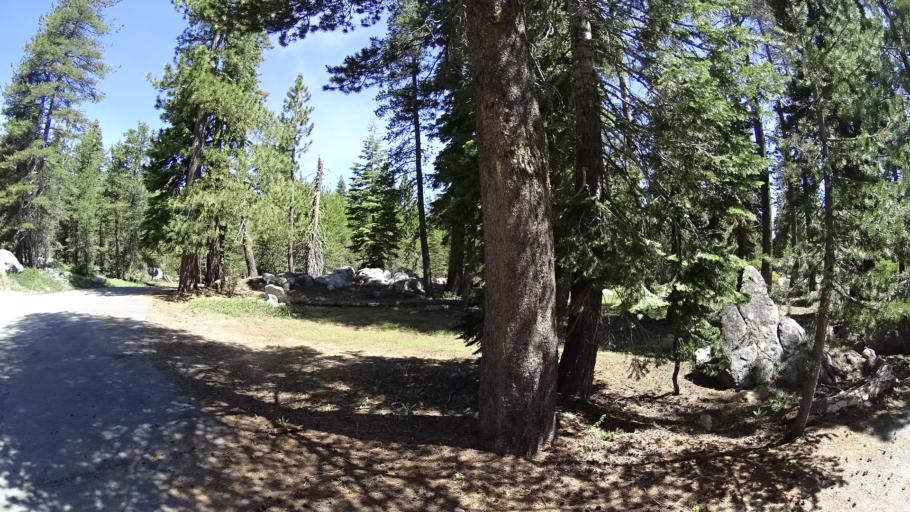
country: US
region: California
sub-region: Calaveras County
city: Arnold
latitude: 38.4395
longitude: -120.0834
